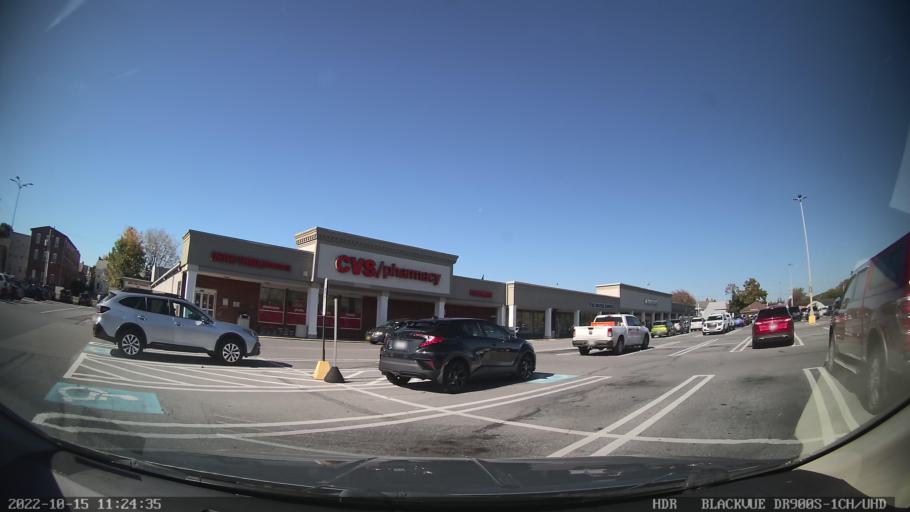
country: US
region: Pennsylvania
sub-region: Berks County
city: Kutztown
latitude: 40.5172
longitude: -75.7745
